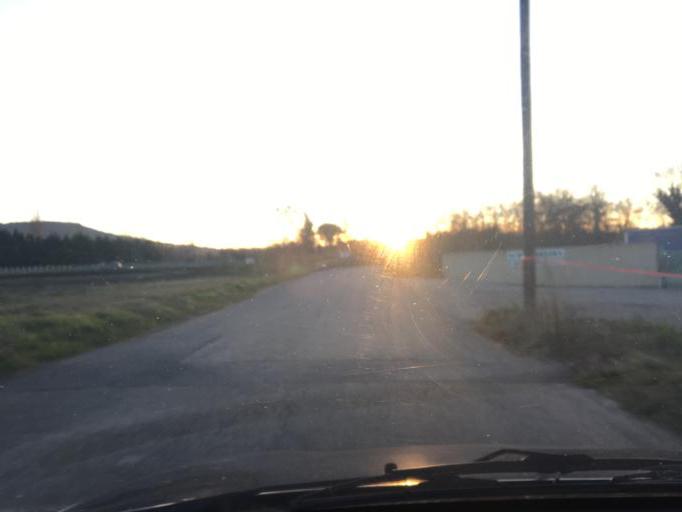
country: FR
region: Provence-Alpes-Cote d'Azur
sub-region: Departement des Bouches-du-Rhone
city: Mallemort
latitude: 43.7196
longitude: 5.1778
